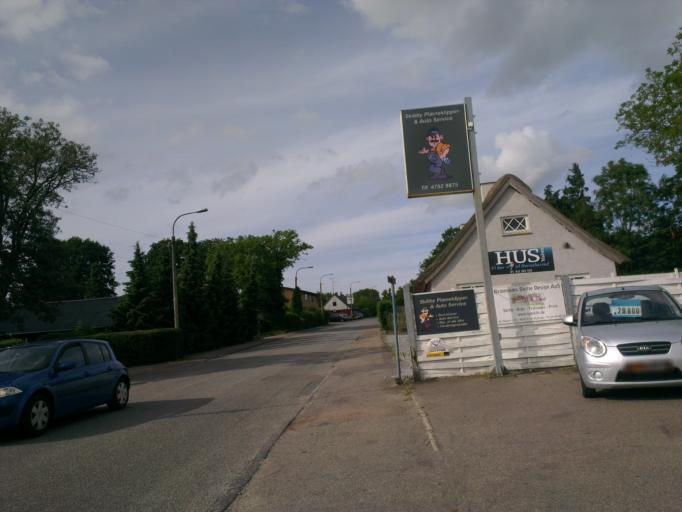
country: DK
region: Capital Region
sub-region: Frederikssund Kommune
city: Skibby
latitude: 55.7452
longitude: 11.9544
